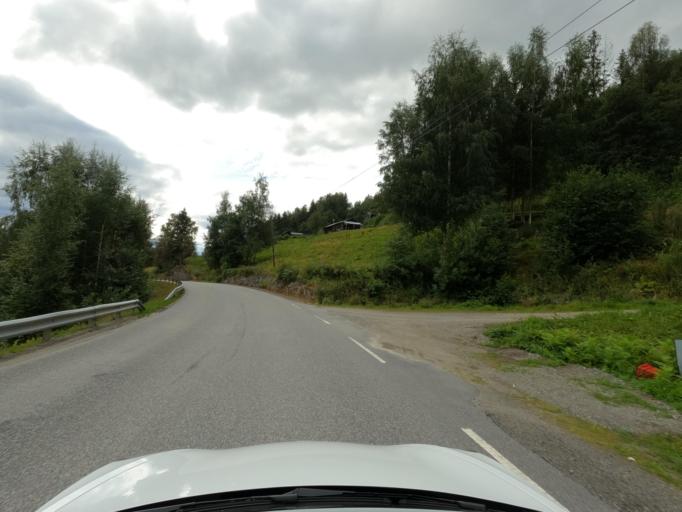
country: NO
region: Telemark
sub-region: Tinn
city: Rjukan
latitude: 59.9579
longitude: 8.8246
